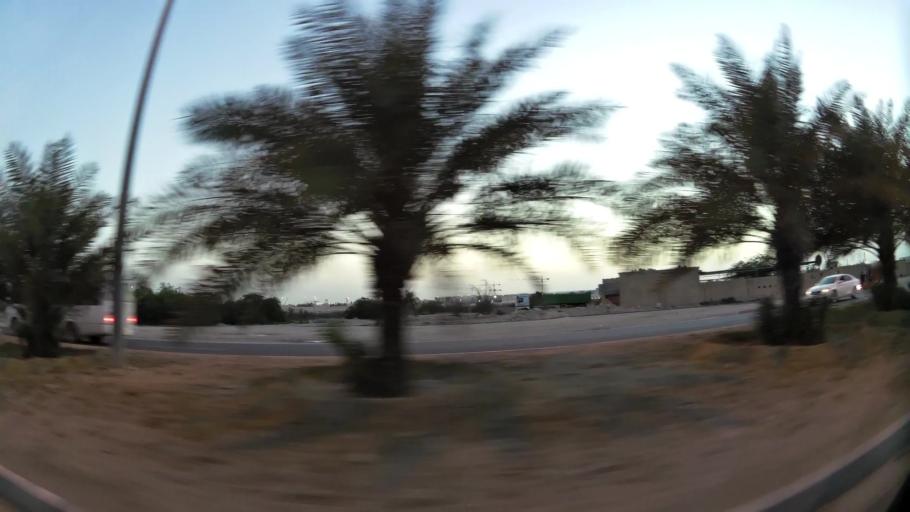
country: QA
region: Baladiyat ar Rayyan
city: Ar Rayyan
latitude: 25.3116
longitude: 51.4610
